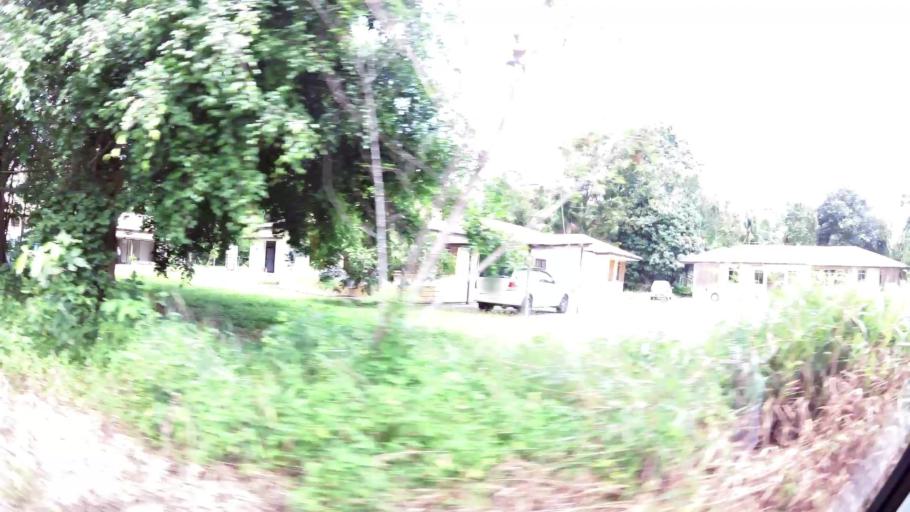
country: BN
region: Brunei and Muara
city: Bandar Seri Begawan
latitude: 4.9013
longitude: 114.9120
